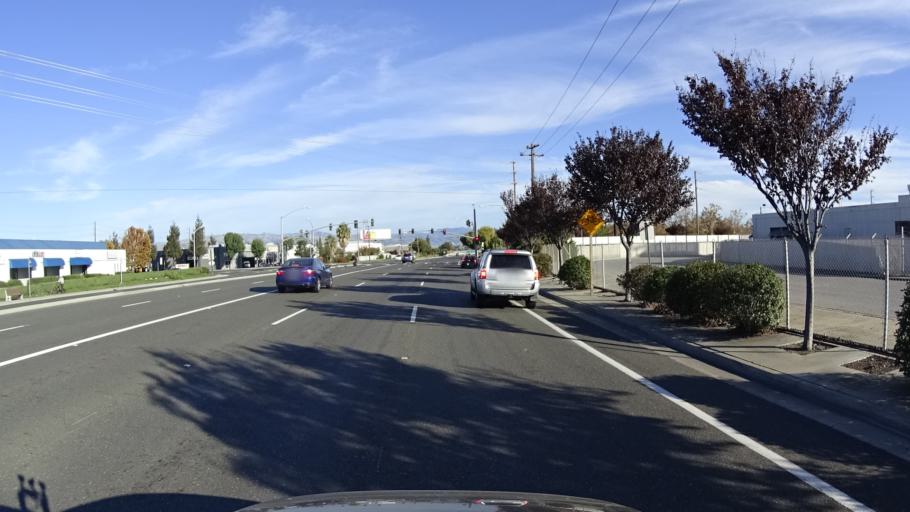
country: US
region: California
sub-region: Santa Clara County
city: Santa Clara
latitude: 37.3743
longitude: -121.9516
